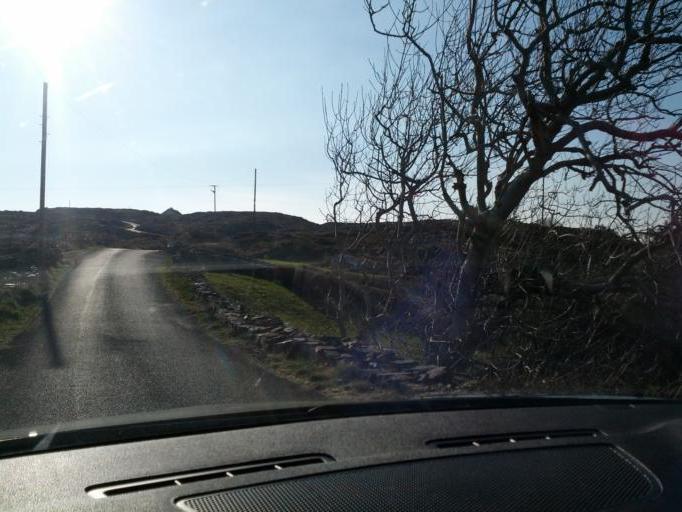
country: IE
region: Connaught
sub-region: County Galway
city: Clifden
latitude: 53.3664
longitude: -9.8682
